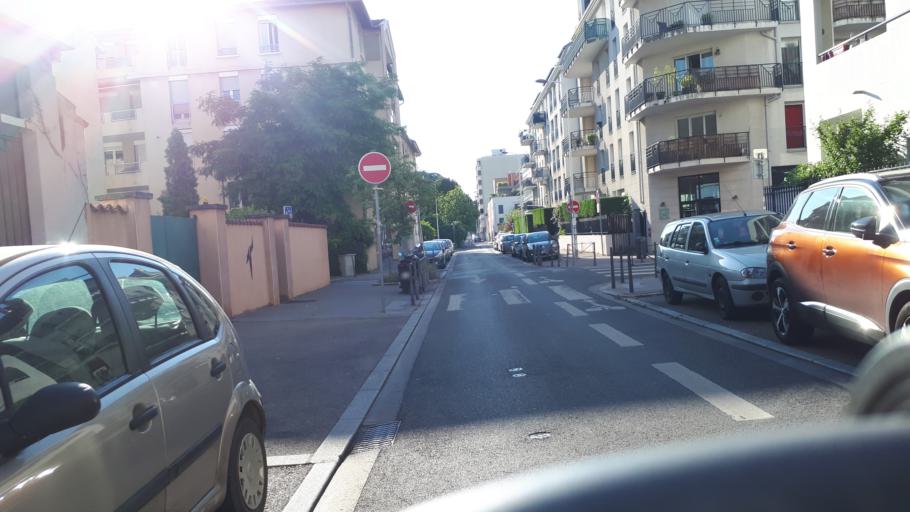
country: FR
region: Rhone-Alpes
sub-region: Departement du Rhone
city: Lyon
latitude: 45.7417
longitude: 4.8714
